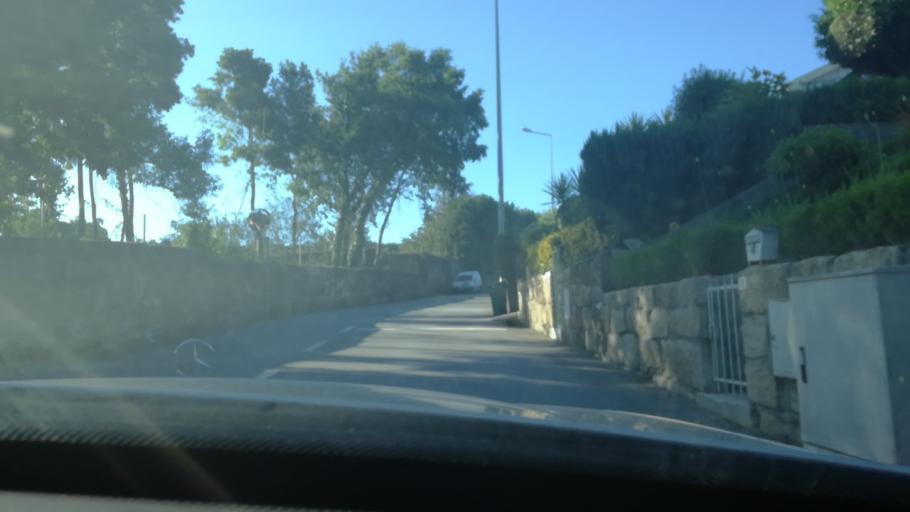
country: PT
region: Porto
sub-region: Maia
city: Leca do Bailio
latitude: 41.2217
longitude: -8.6238
